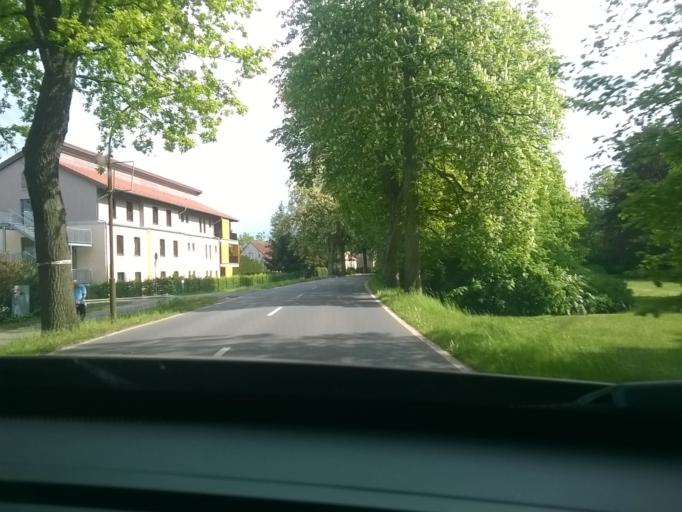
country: DE
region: Brandenburg
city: Wittstock
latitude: 53.1510
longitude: 12.4874
